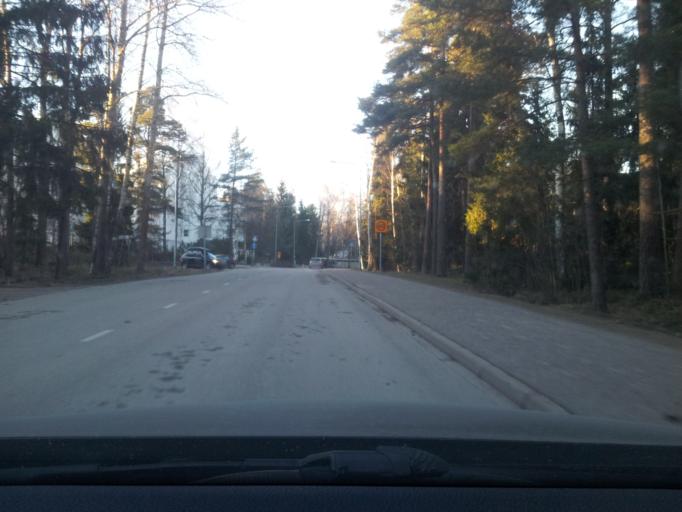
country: FI
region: Uusimaa
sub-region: Helsinki
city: Koukkuniemi
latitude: 60.1592
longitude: 24.7902
